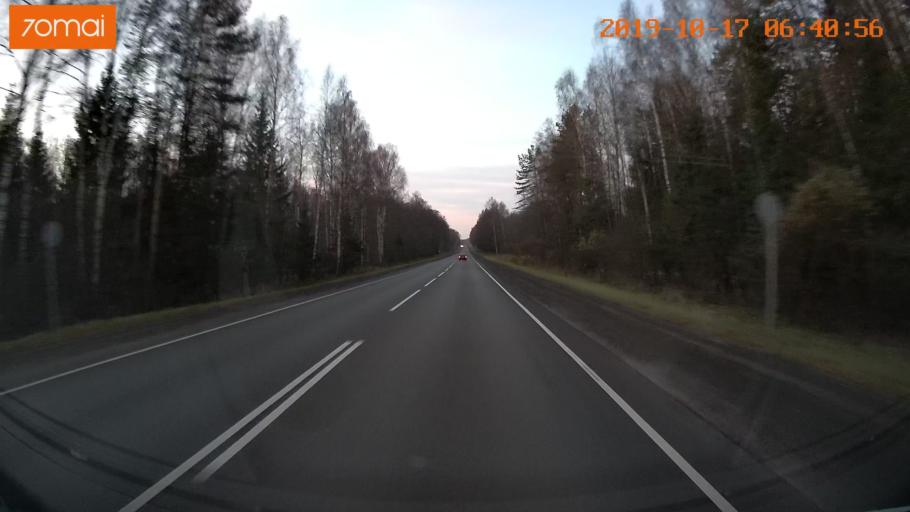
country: RU
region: Ivanovo
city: Nerl'
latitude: 56.6220
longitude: 40.5648
